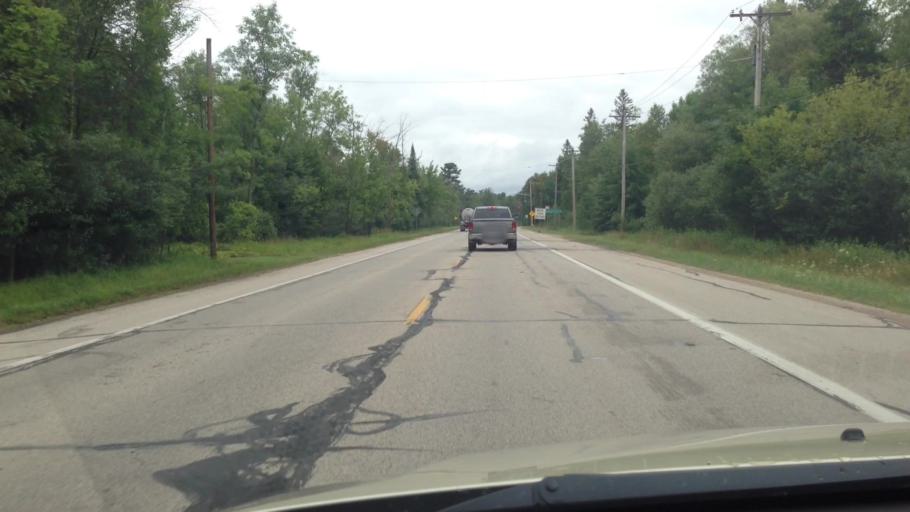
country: US
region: Michigan
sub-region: Delta County
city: Escanaba
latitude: 45.6992
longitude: -87.1014
